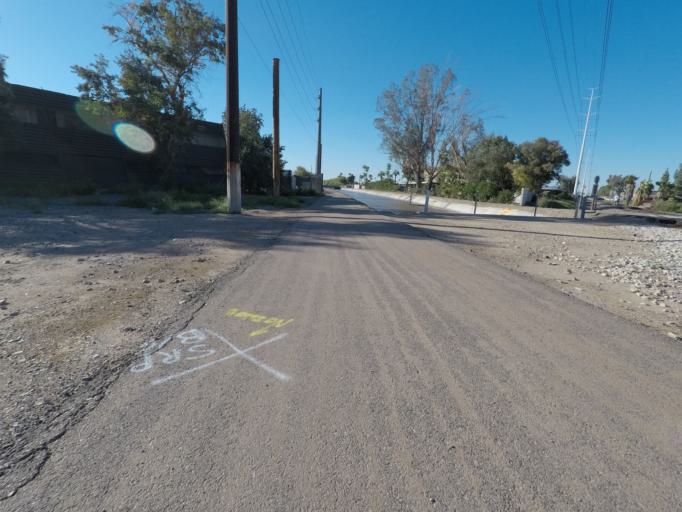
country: US
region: Arizona
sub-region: Maricopa County
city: Guadalupe
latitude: 33.3764
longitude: -111.9435
